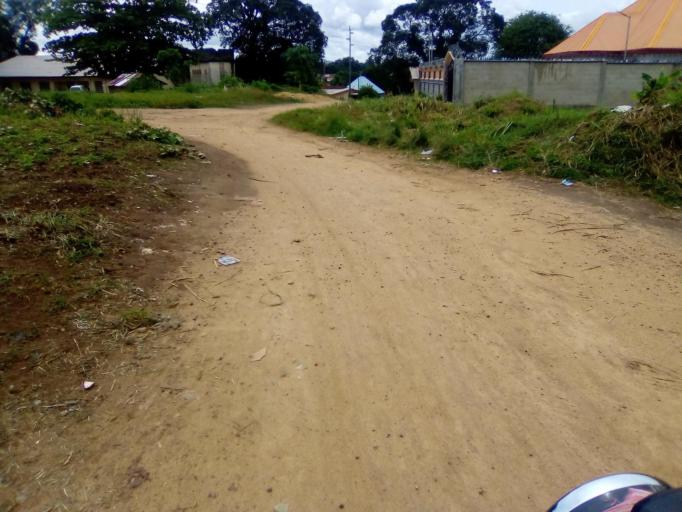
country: SL
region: Southern Province
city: Bo
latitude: 7.9473
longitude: -11.7274
